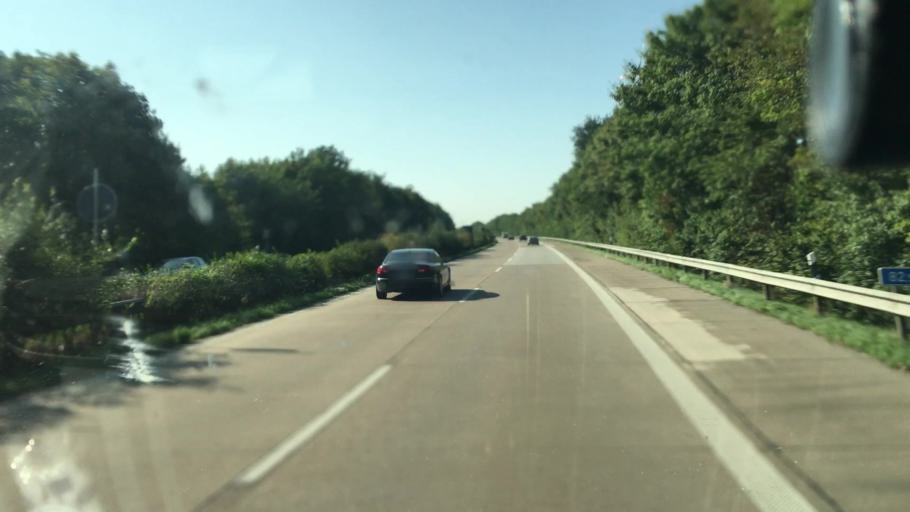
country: DE
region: Lower Saxony
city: Sande
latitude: 53.5121
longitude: 7.9966
